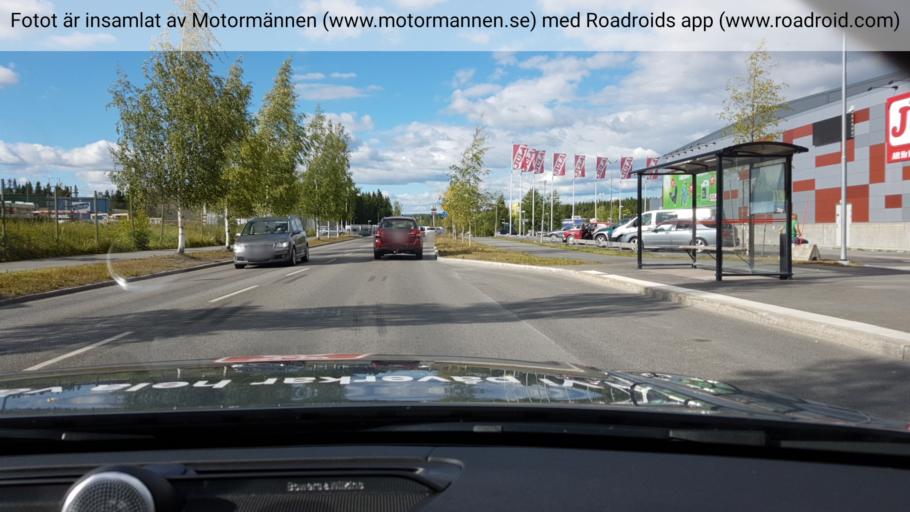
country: SE
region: Jaemtland
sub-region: OEstersunds Kommun
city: Ostersund
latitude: 63.1736
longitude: 14.6908
